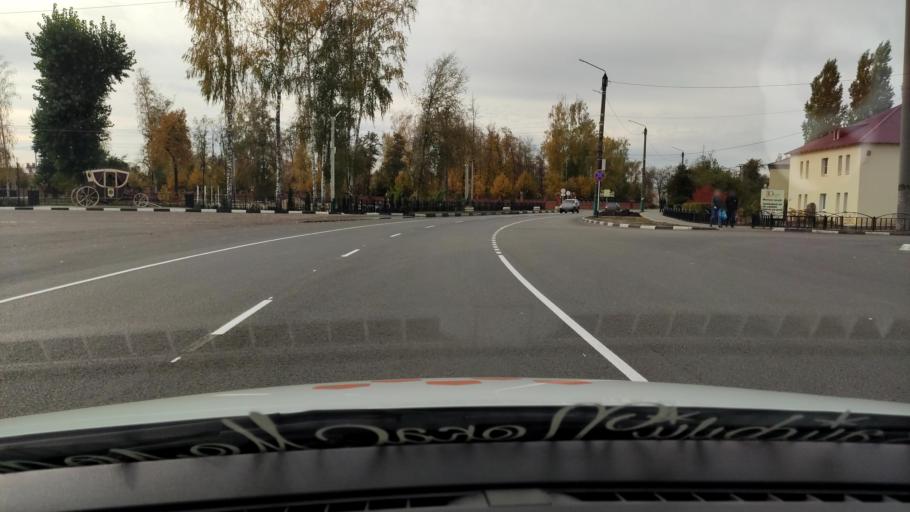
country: RU
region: Voronezj
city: Ramon'
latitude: 51.9108
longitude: 39.3383
